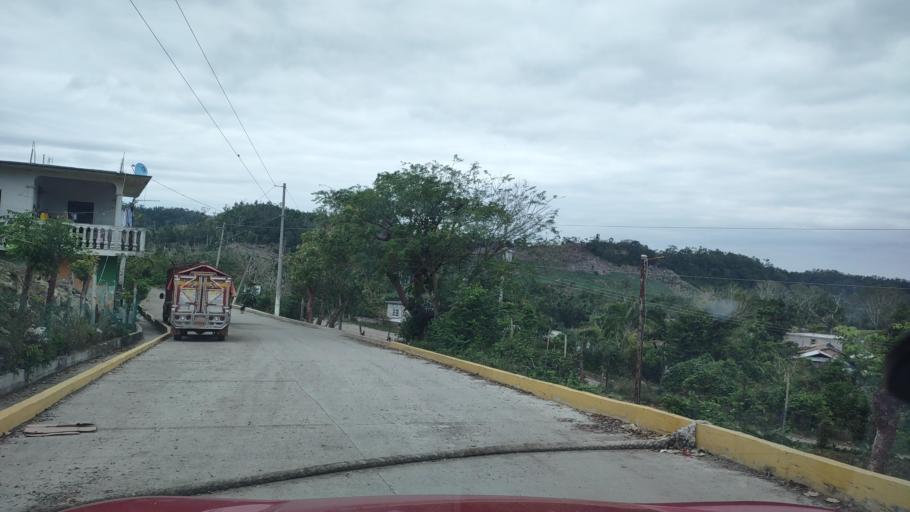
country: MX
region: Veracruz
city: Papantla de Olarte
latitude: 20.4218
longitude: -97.2710
